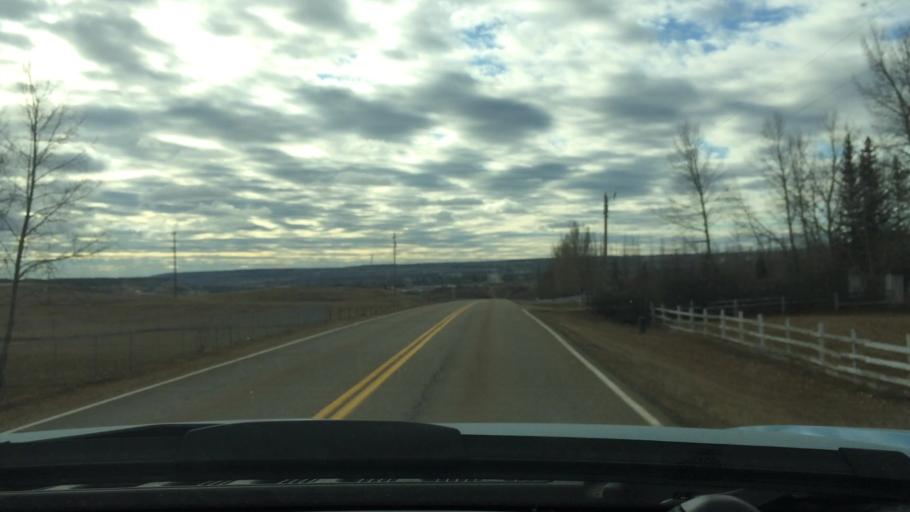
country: CA
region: Alberta
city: Airdrie
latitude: 51.1996
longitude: -114.1412
